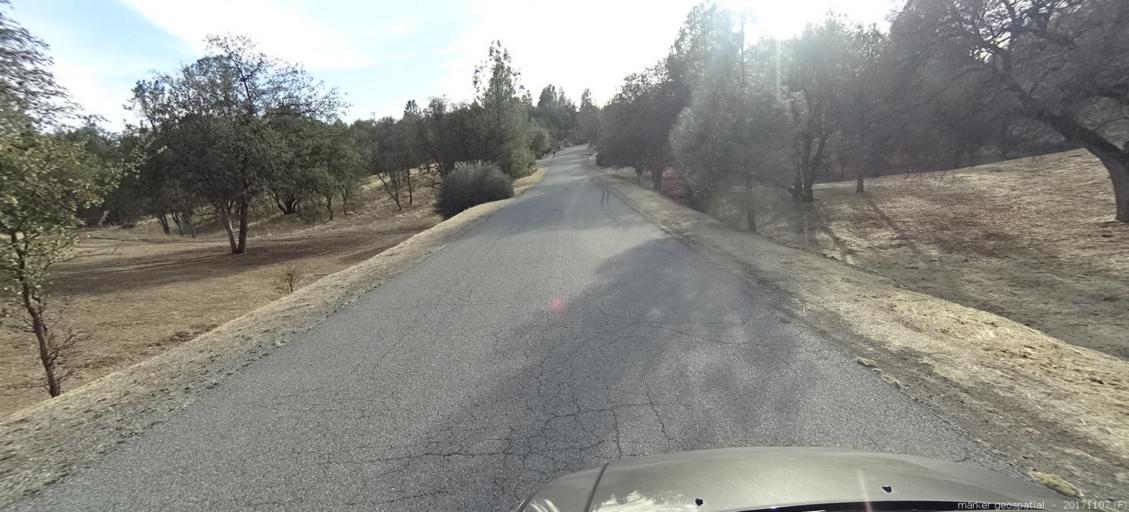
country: US
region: California
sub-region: Shasta County
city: Shasta
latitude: 40.5109
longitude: -122.4699
